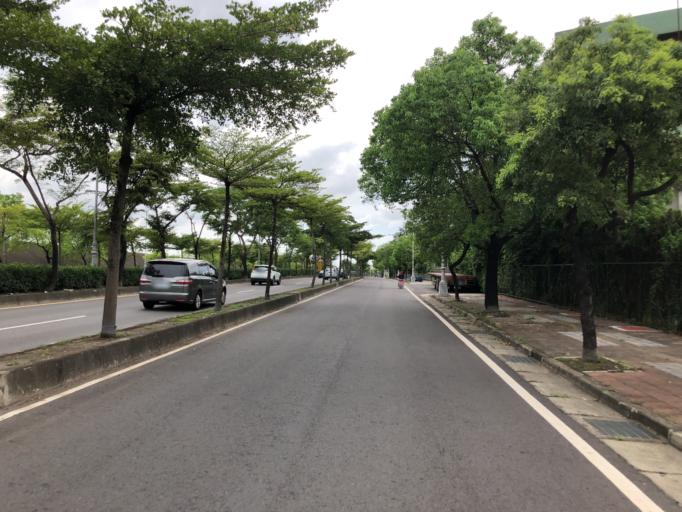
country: TW
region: Taiwan
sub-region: Taichung City
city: Taichung
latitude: 24.0936
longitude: 120.6421
